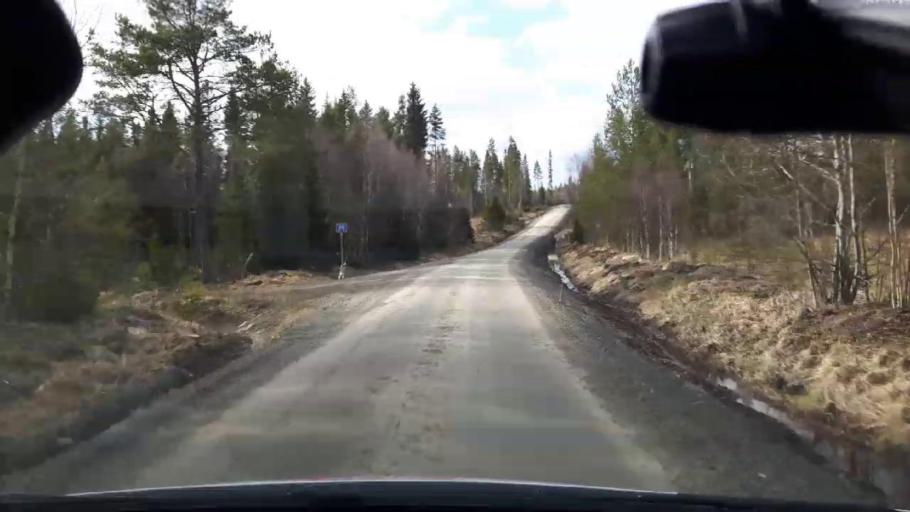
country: SE
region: Jaemtland
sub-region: Bergs Kommun
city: Hoverberg
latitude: 62.8943
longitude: 14.6530
